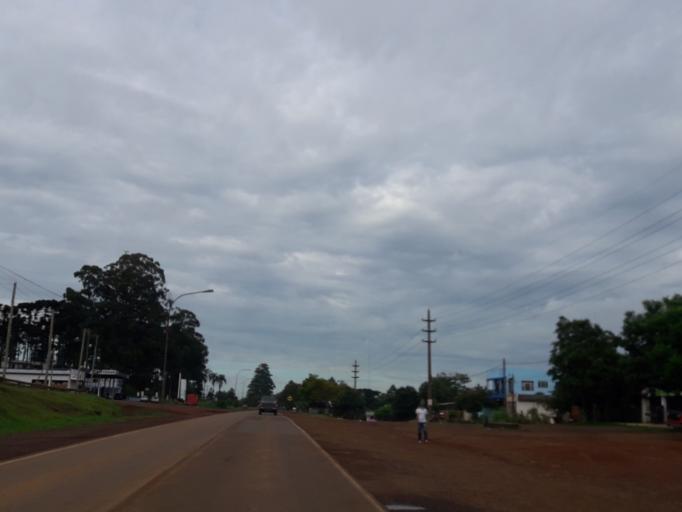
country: AR
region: Misiones
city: Bernardo de Irigoyen
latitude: -26.2615
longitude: -53.6495
